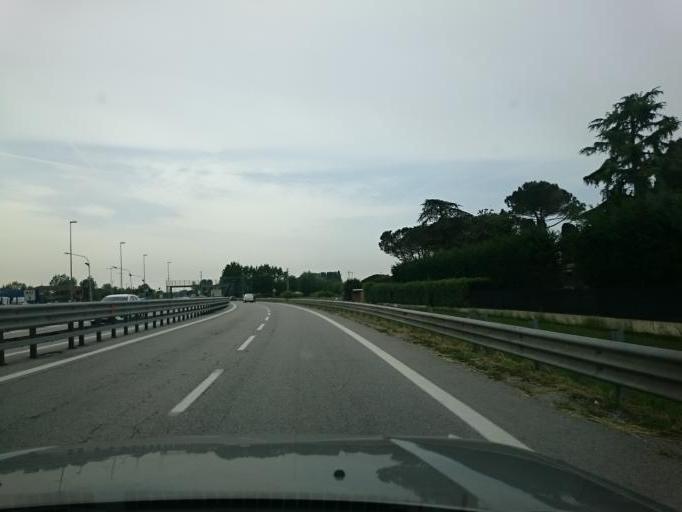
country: IT
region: Veneto
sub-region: Provincia di Venezia
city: Campalto
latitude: 45.5065
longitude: 12.2704
